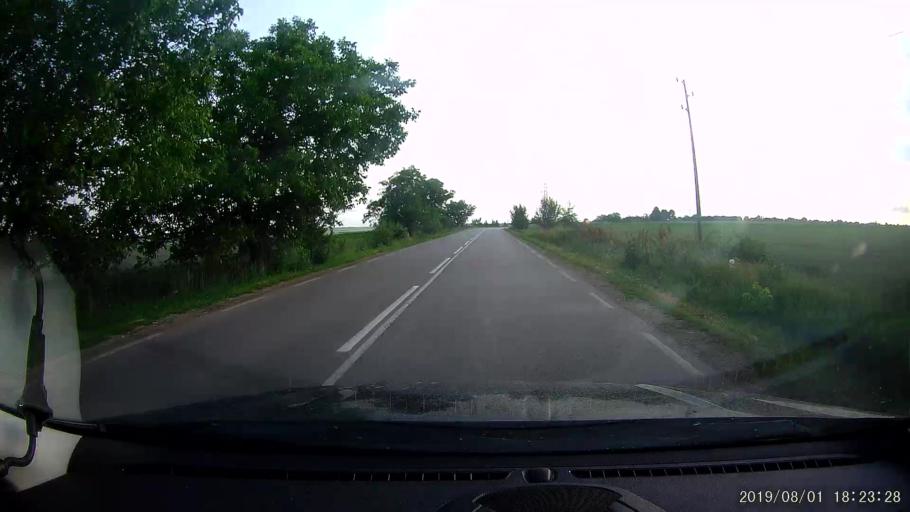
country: BG
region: Shumen
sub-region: Obshtina Kaolinovo
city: Kaolinovo
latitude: 43.6286
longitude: 27.0245
